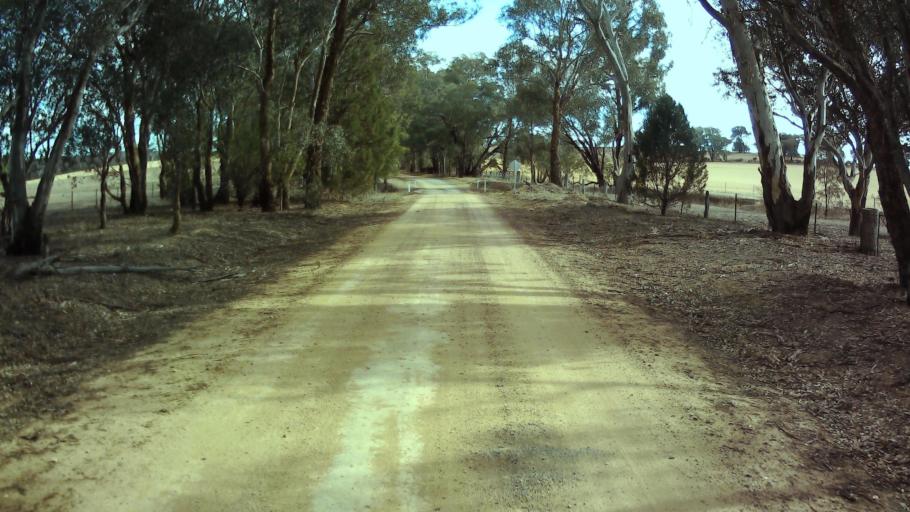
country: AU
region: New South Wales
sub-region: Weddin
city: Grenfell
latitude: -33.9005
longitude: 148.2031
